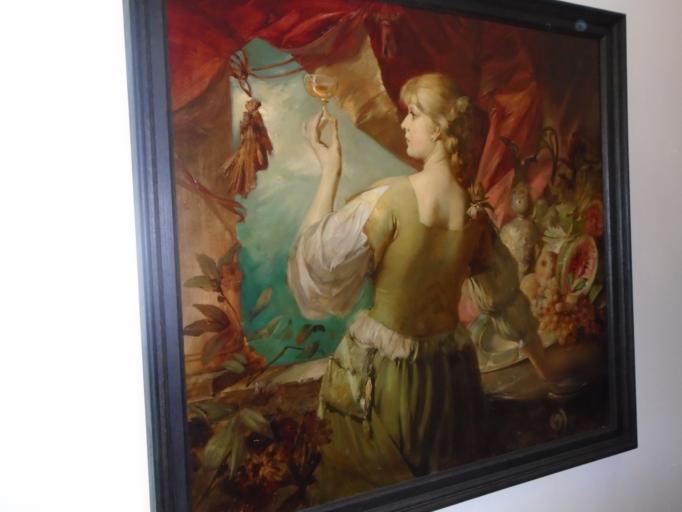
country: CZ
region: Moravskoslezsky
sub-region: Okres Novy Jicin
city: Novy Jicin
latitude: 49.5959
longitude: 18.0087
